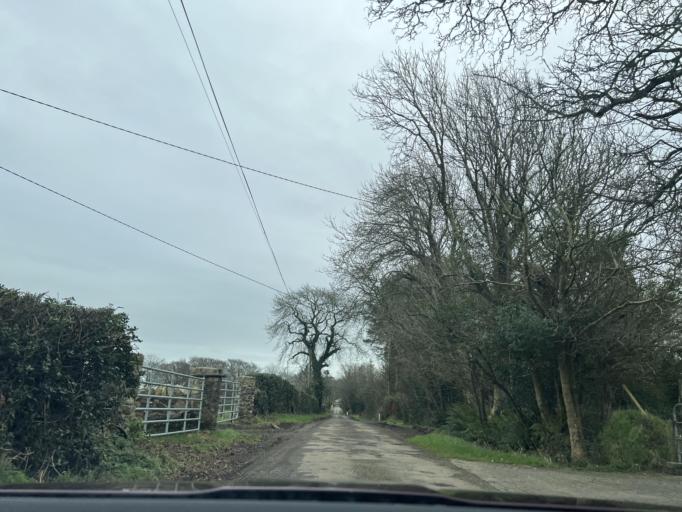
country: IE
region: Leinster
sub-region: Loch Garman
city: Castlebridge
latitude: 52.3888
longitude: -6.5396
